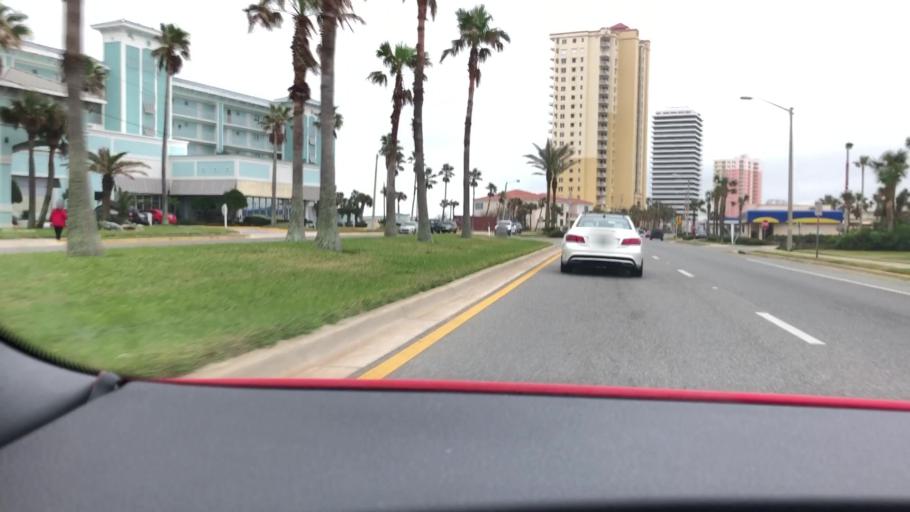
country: US
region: Florida
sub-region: Volusia County
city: Holly Hill
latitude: 29.2617
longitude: -81.0252
